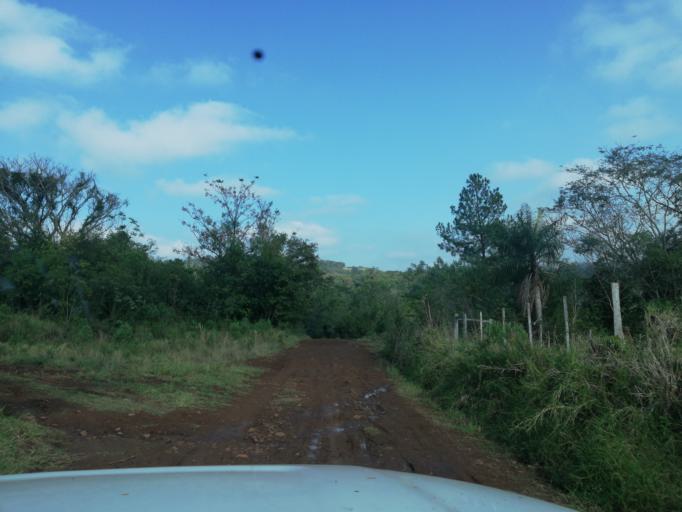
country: AR
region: Misiones
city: Cerro Azul
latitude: -27.6006
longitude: -55.5300
